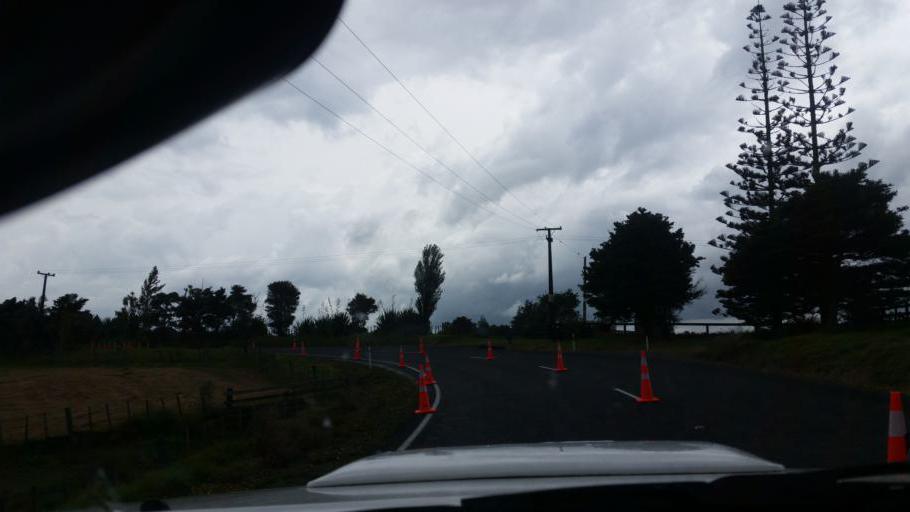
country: NZ
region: Auckland
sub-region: Auckland
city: Wellsford
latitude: -36.1466
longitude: 174.2238
